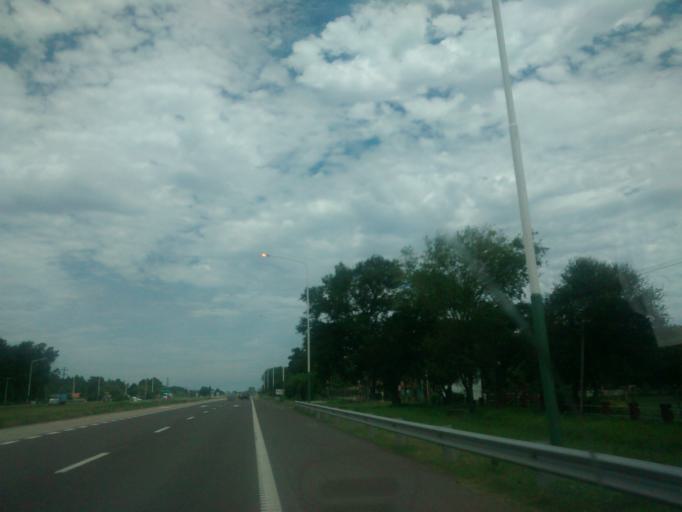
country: AR
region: Chaco
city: Fontana
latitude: -27.4006
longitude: -59.0153
